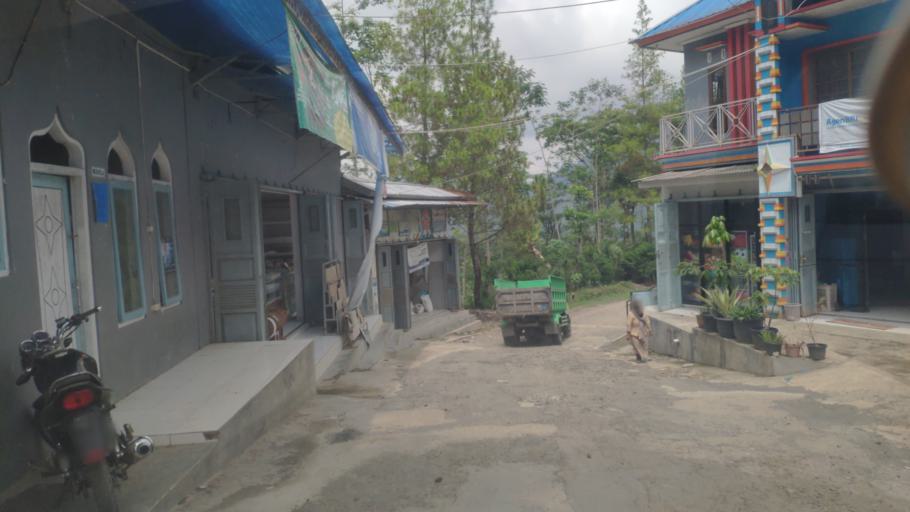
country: ID
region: Central Java
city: Wonosobo
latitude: -7.3197
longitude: 109.7853
